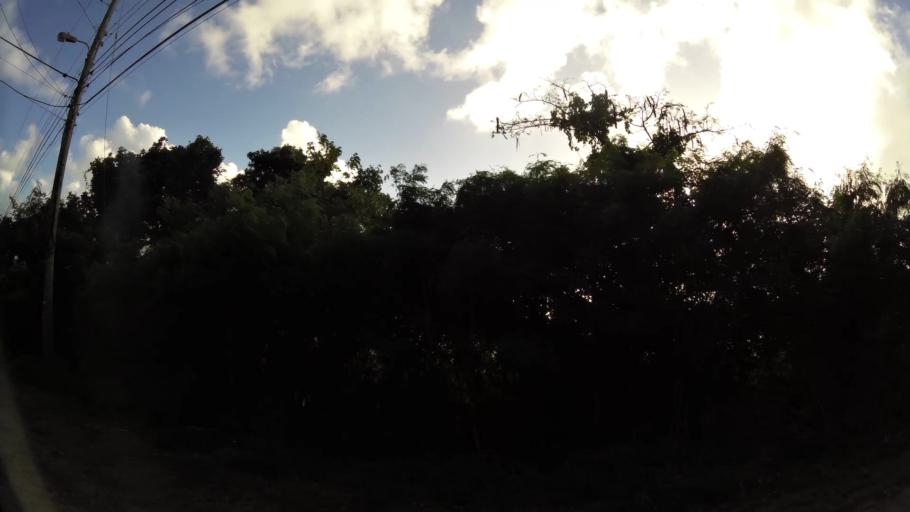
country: LC
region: Gros-Islet
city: Gros Islet
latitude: 14.1031
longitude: -60.9361
